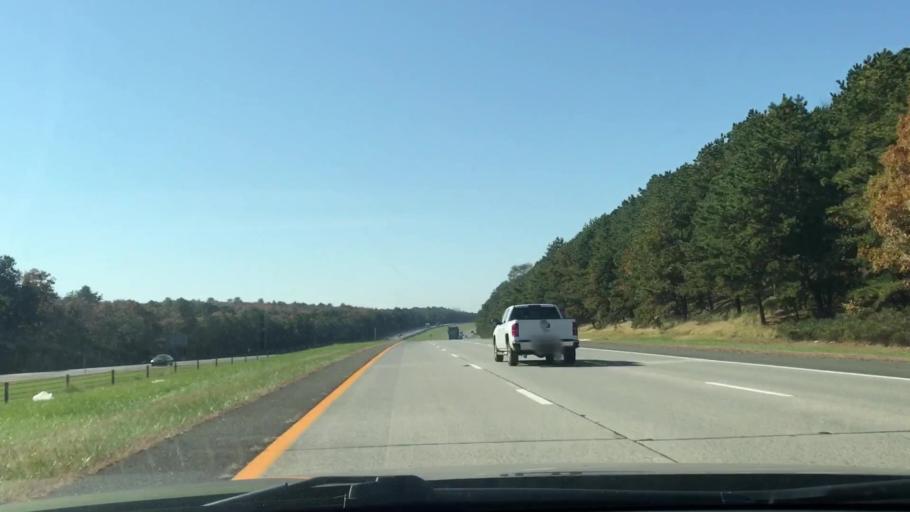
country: US
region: New York
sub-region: Suffolk County
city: Calverton
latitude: 40.8850
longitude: -72.7631
